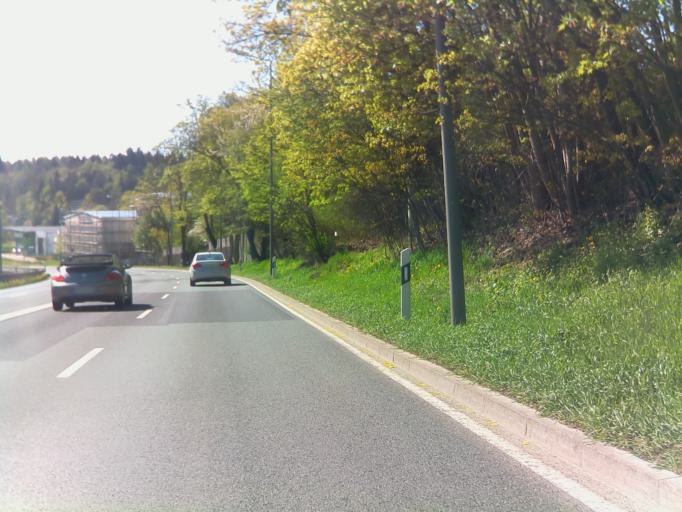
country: DE
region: Saxony
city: Plauen
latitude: 50.5233
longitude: 12.1119
